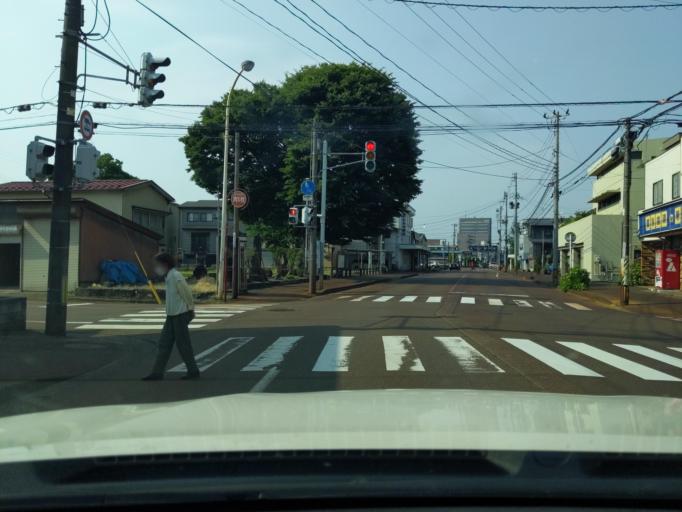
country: JP
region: Niigata
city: Nagaoka
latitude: 37.4403
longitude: 138.8555
